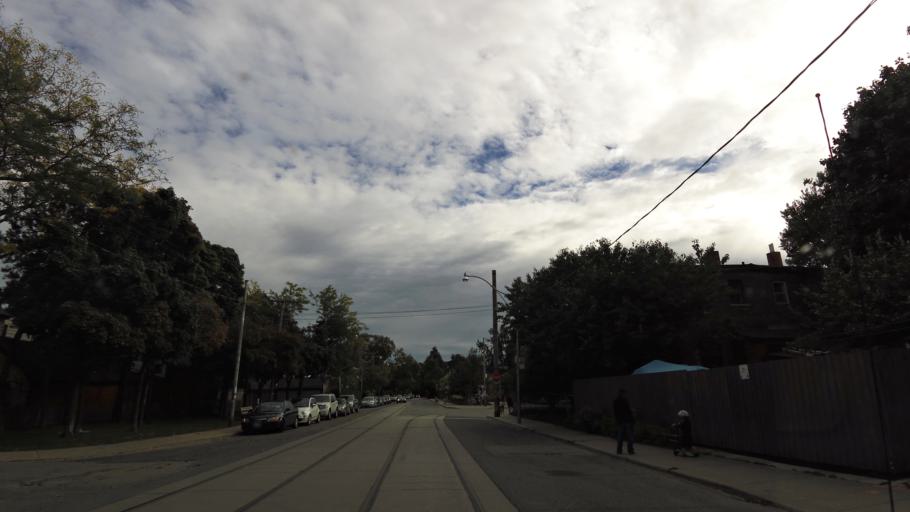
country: CA
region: Ontario
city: Toronto
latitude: 43.6809
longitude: -79.4230
